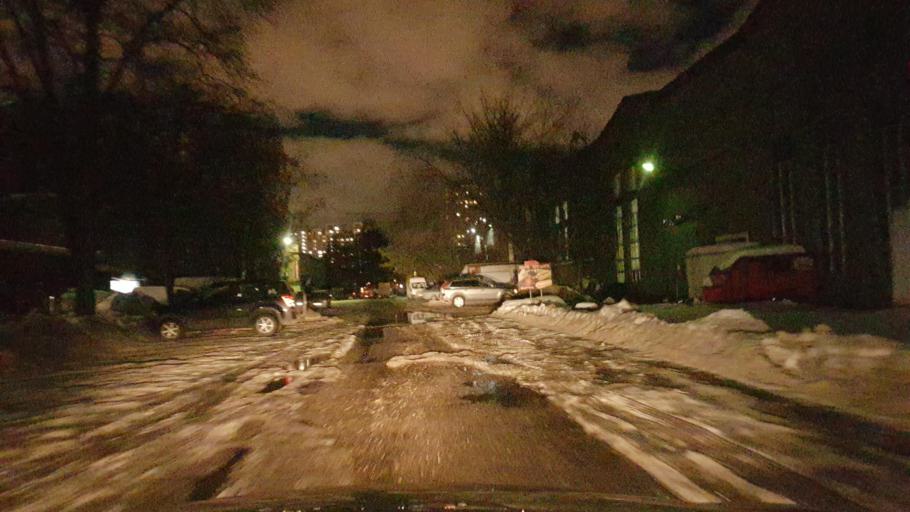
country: RU
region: Moscow
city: Pokrovskoye-Streshnevo
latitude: 55.8409
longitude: 37.4486
